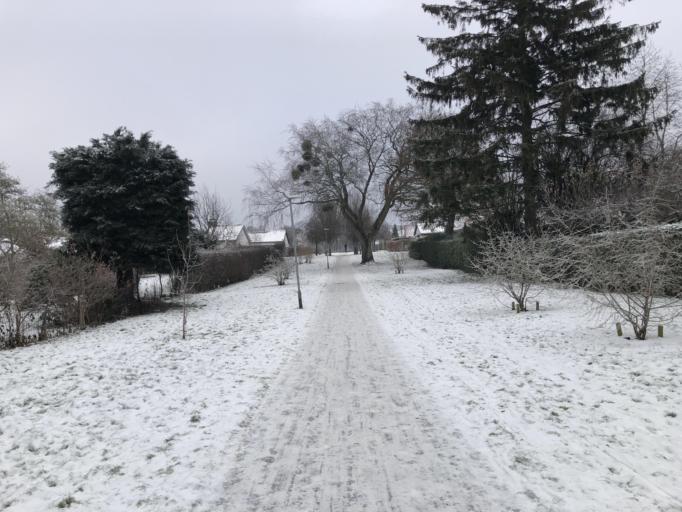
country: DK
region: Capital Region
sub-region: Rudersdal Kommune
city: Holte
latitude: 55.7853
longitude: 12.4644
